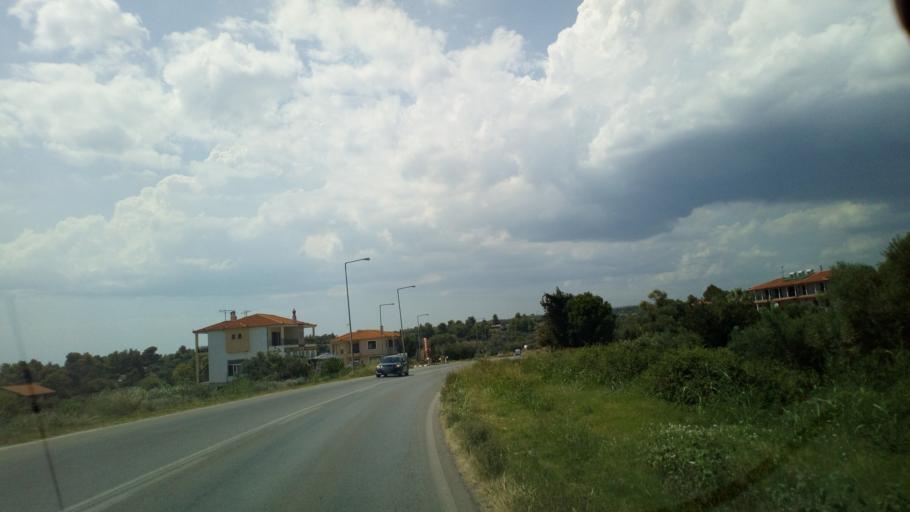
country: GR
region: Central Macedonia
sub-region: Nomos Chalkidikis
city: Nikiti
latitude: 40.2269
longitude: 23.6503
